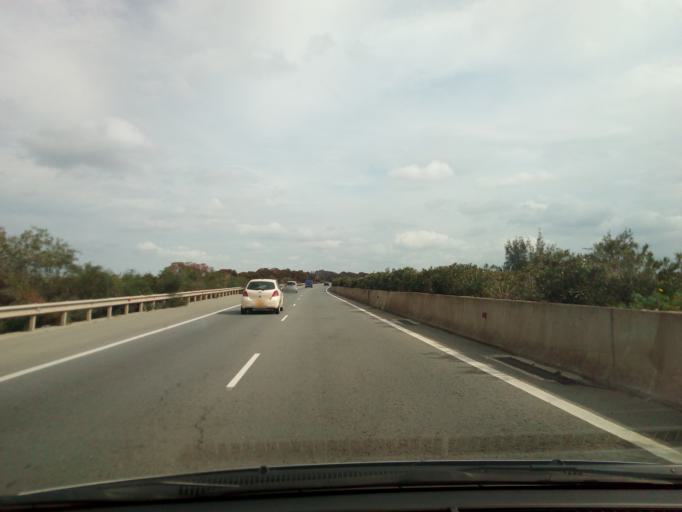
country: CY
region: Lefkosia
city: Kokkinotrimithia
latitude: 35.1451
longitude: 33.2608
